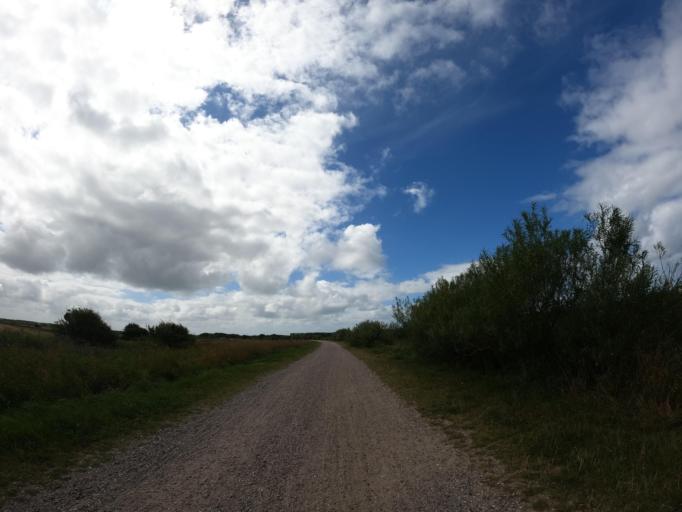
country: DE
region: Schleswig-Holstein
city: Tinnum
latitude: 54.8959
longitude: 8.3225
